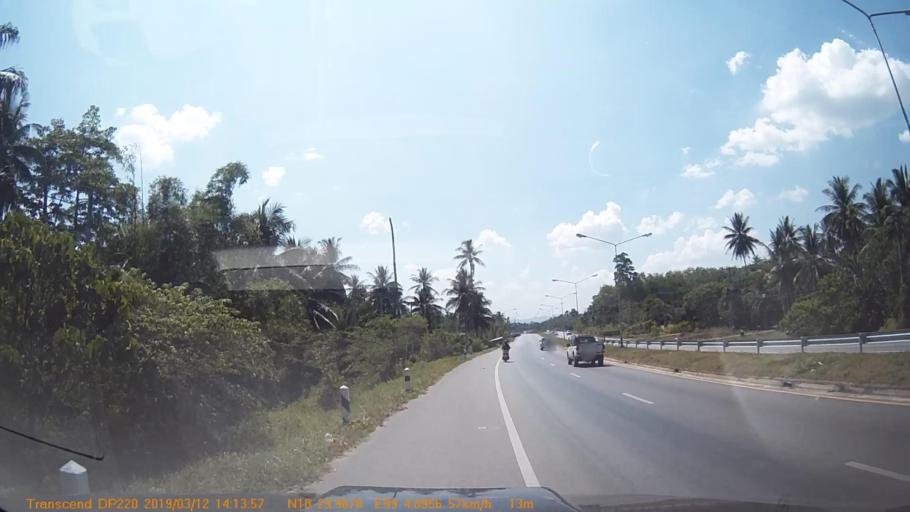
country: TH
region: Chumphon
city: Chumphon
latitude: 10.4994
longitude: 99.0813
